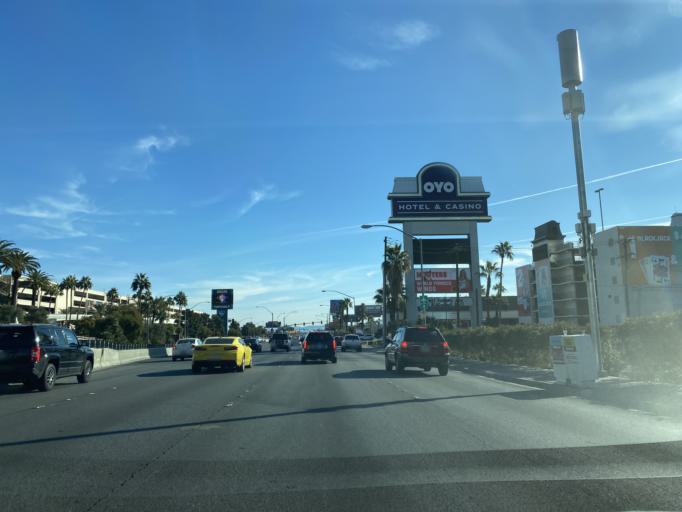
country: US
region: Nevada
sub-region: Clark County
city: Paradise
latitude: 36.1008
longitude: -115.1691
